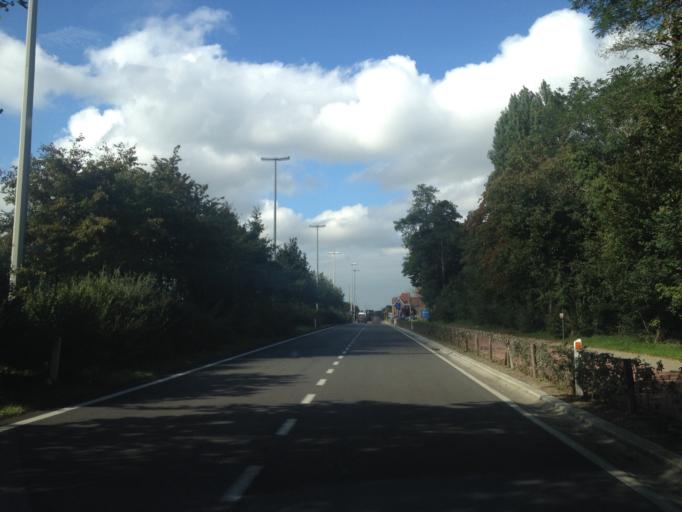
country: BE
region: Flanders
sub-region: Provincie West-Vlaanderen
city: Brugge
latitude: 51.1983
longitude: 3.1957
